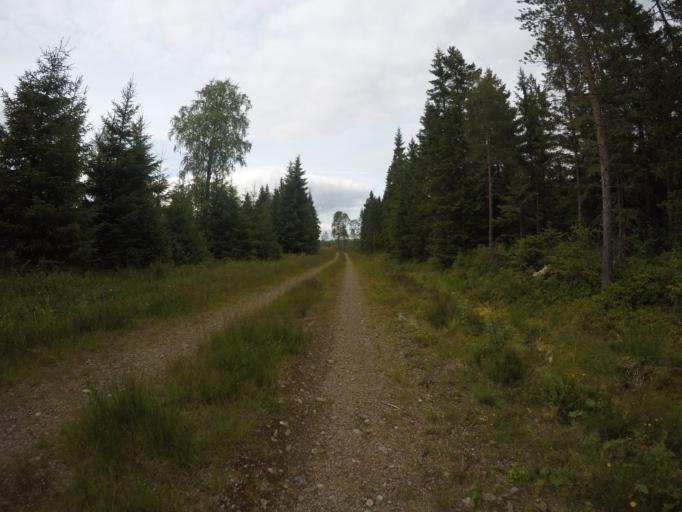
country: SE
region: Vaermland
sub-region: Filipstads Kommun
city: Lesjofors
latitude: 60.2011
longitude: 14.2596
